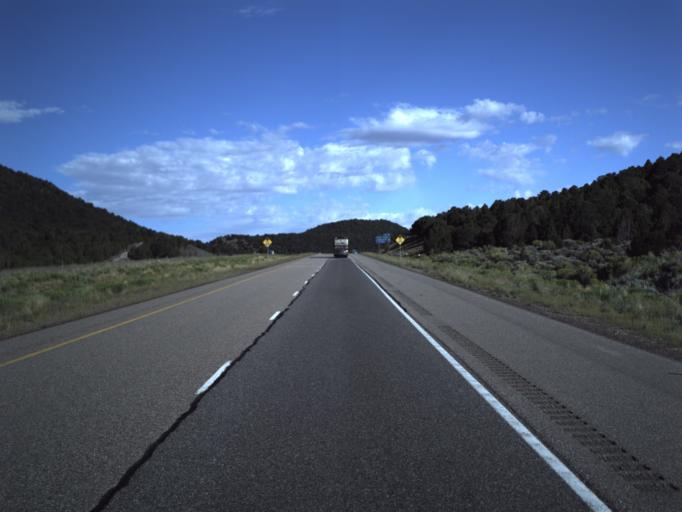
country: US
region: Utah
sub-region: Beaver County
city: Beaver
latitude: 38.5822
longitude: -112.4838
